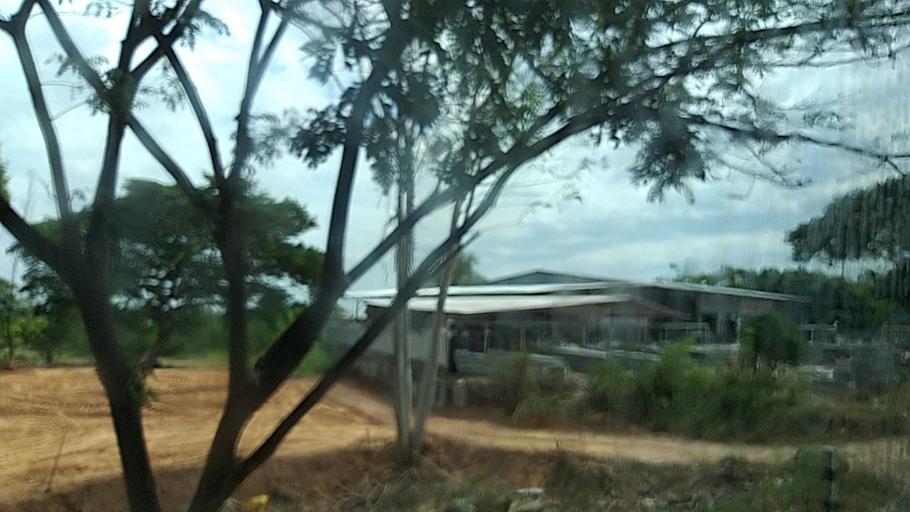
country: TH
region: Maha Sarakham
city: Chiang Yuen
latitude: 16.3710
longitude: 103.1060
